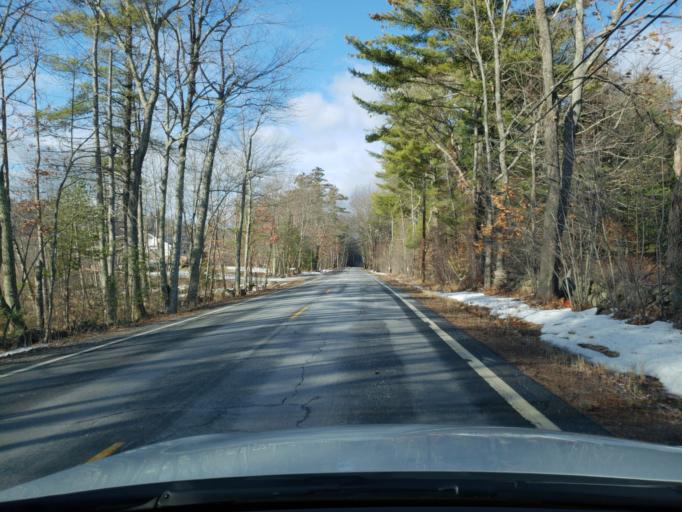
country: US
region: New Hampshire
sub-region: Hillsborough County
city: New Boston
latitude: 42.9955
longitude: -71.7496
